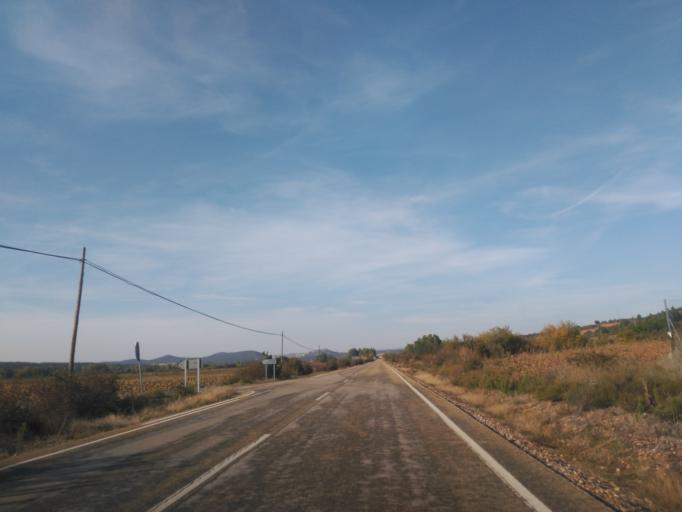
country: ES
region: Castille and Leon
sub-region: Provincia de Soria
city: Valdemaluque
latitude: 41.6591
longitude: -3.0507
